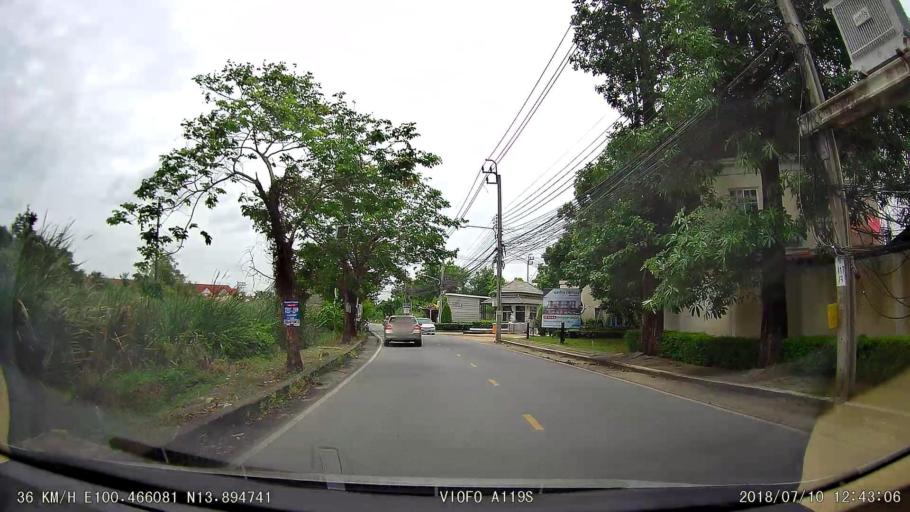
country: TH
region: Nonthaburi
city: Pak Kret
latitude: 13.8948
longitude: 100.4662
